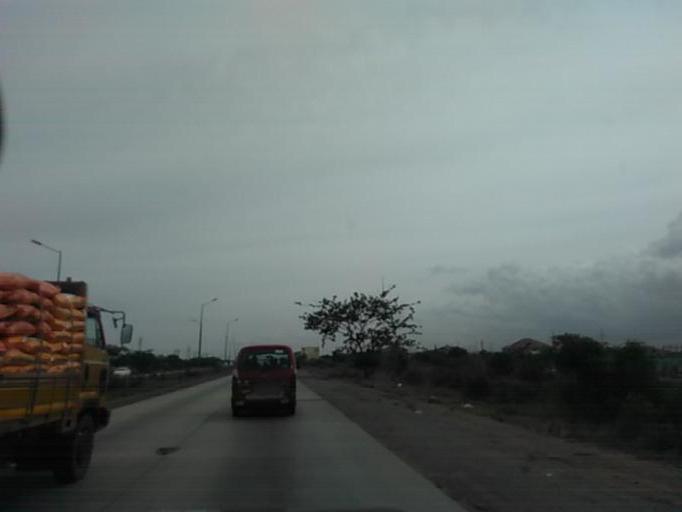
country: GH
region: Greater Accra
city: Nungua
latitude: 5.6559
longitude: -0.0916
